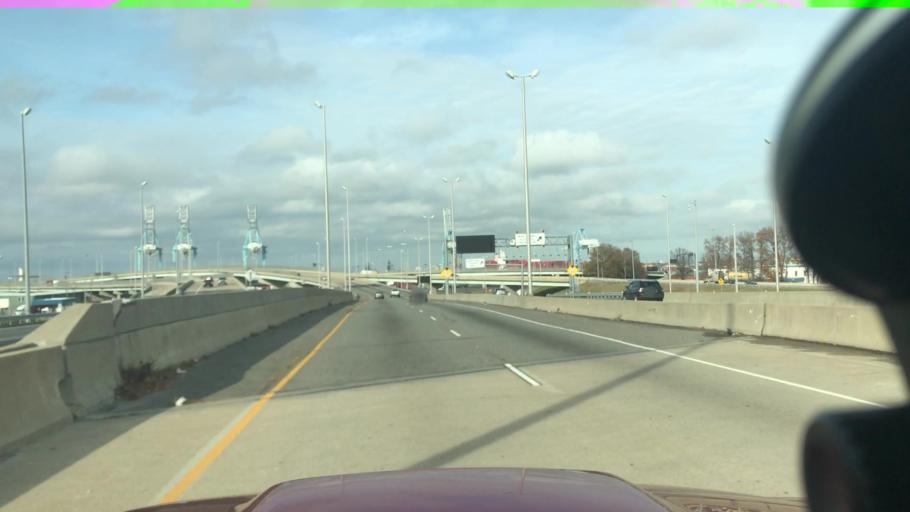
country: US
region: Virginia
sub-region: City of Portsmouth
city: Portsmouth
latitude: 36.8472
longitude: -76.3294
